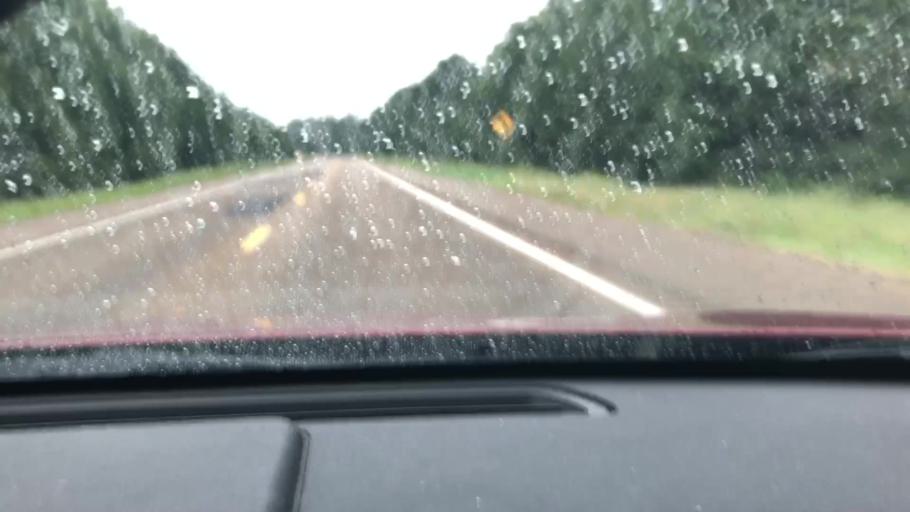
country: US
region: Arkansas
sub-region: Columbia County
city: Magnolia
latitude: 33.3012
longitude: -93.2675
